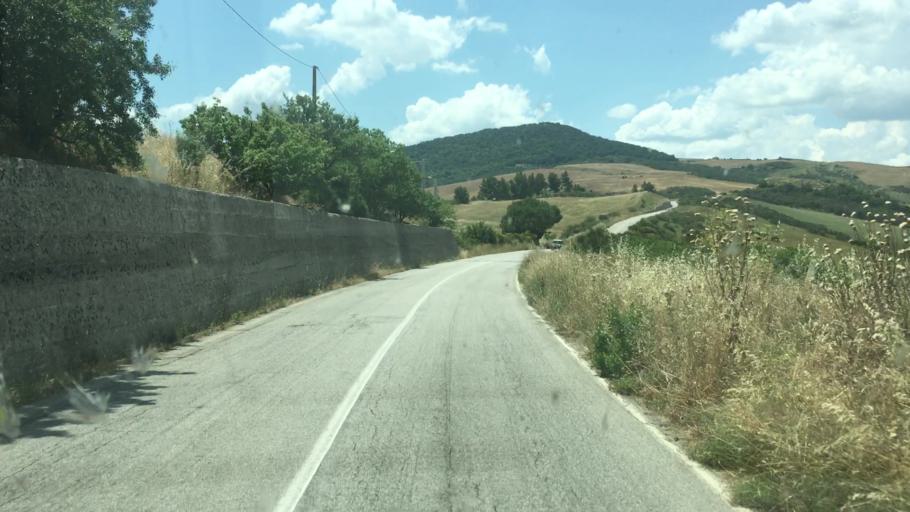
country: IT
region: Basilicate
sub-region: Provincia di Potenza
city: Tolve
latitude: 40.6965
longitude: 15.9930
